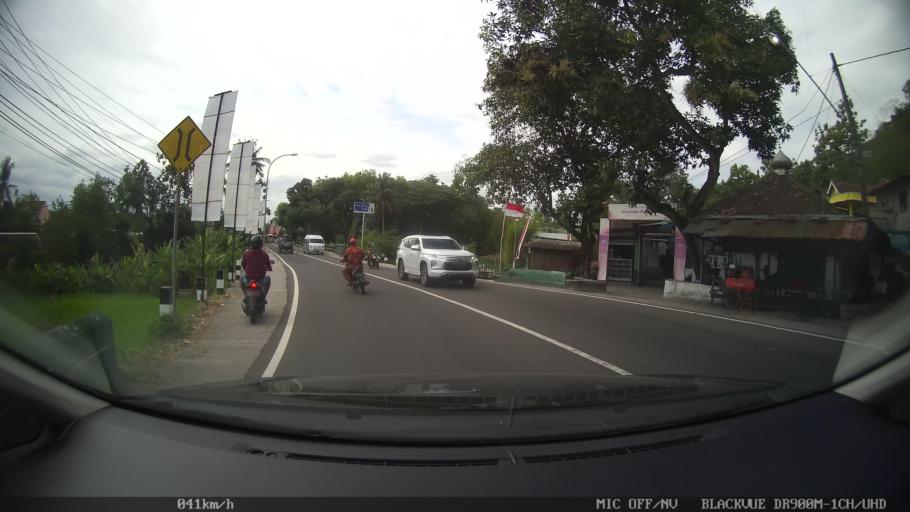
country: ID
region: Central Java
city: Candi Prambanan
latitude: -7.7681
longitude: 110.4876
